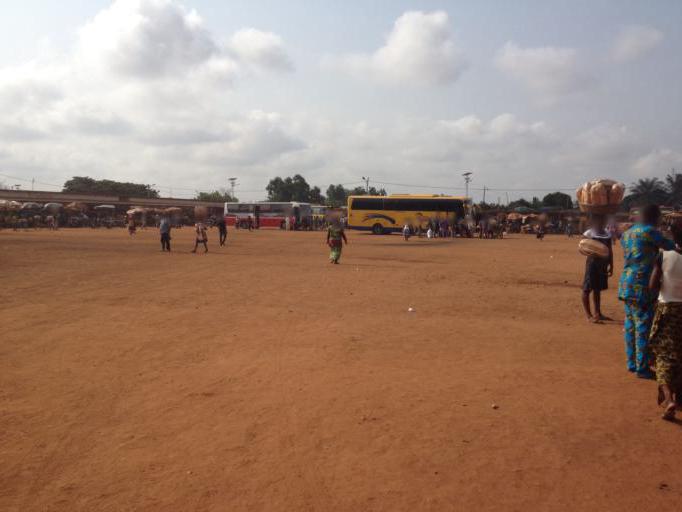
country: BJ
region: Zou
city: Bohicon
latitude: 7.1828
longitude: 2.0908
